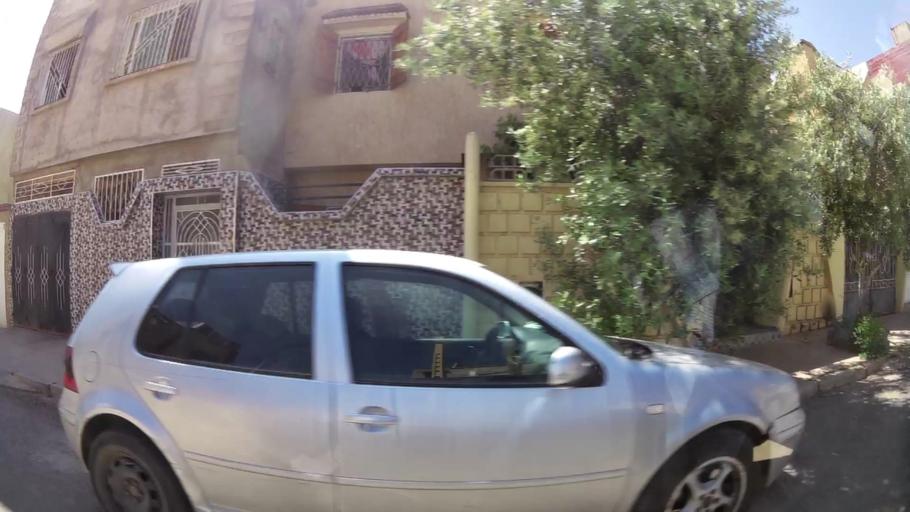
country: MA
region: Oriental
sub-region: Oujda-Angad
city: Oujda
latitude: 34.6689
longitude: -1.9485
